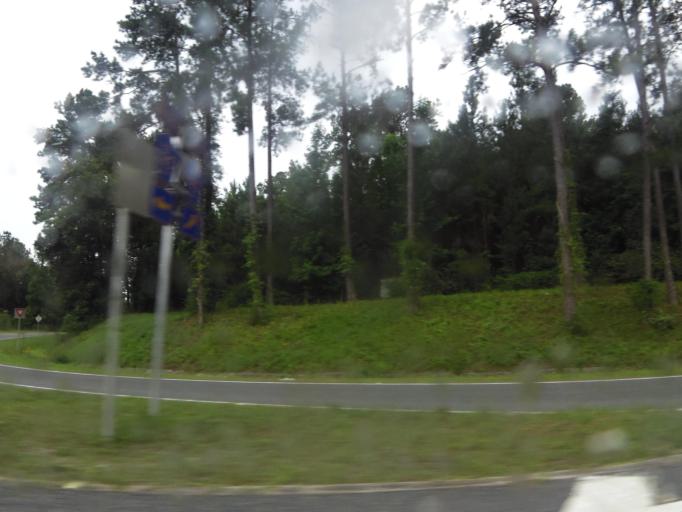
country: US
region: Florida
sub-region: Baker County
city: Macclenny
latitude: 30.2606
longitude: -82.1625
